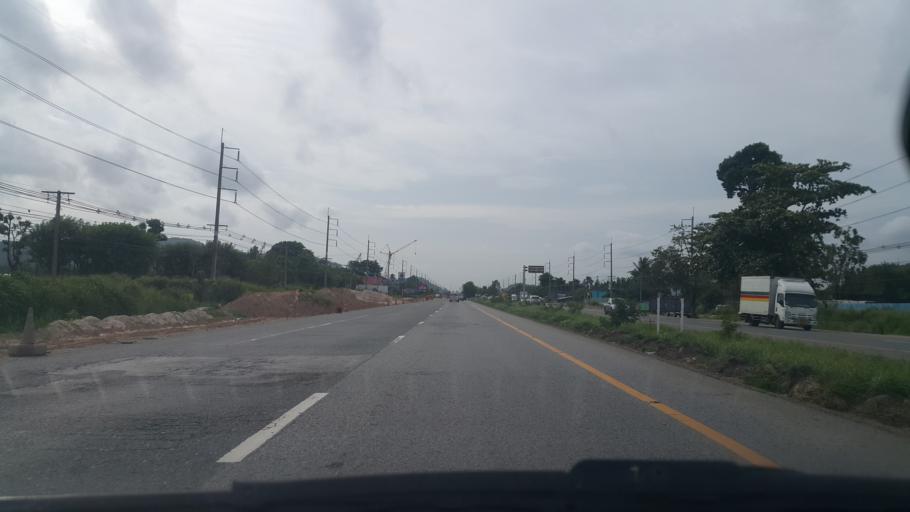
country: TH
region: Rayong
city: Nikhom Phattana
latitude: 12.7992
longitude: 101.1491
